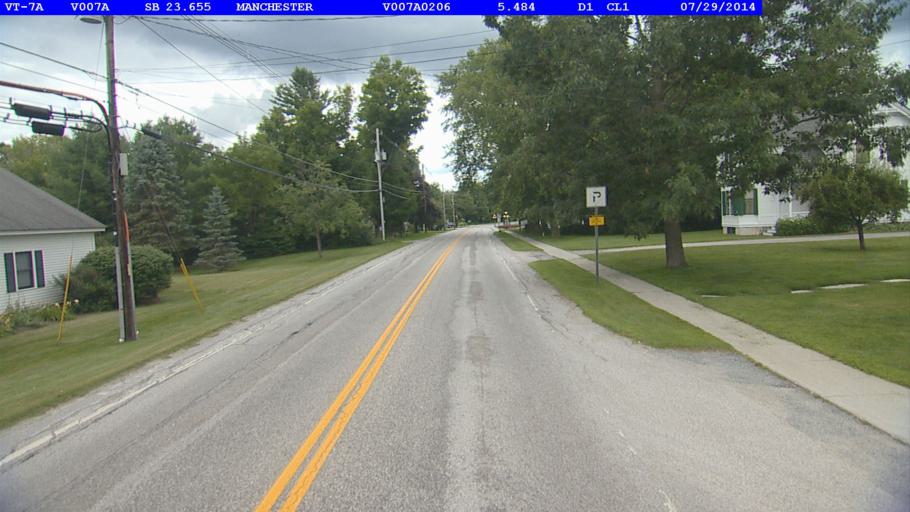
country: US
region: Vermont
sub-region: Bennington County
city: Manchester Center
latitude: 43.1809
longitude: -73.0471
